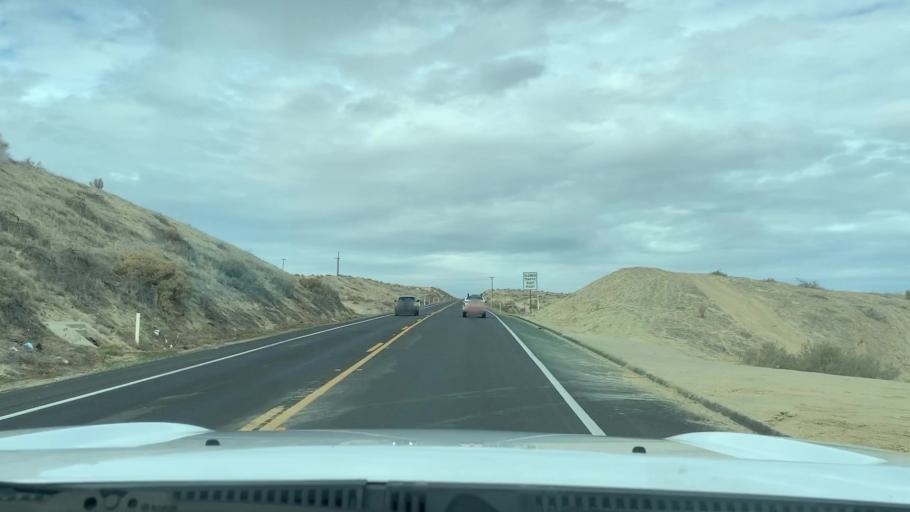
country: US
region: California
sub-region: Kern County
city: Maricopa
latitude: 35.0991
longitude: -119.4139
